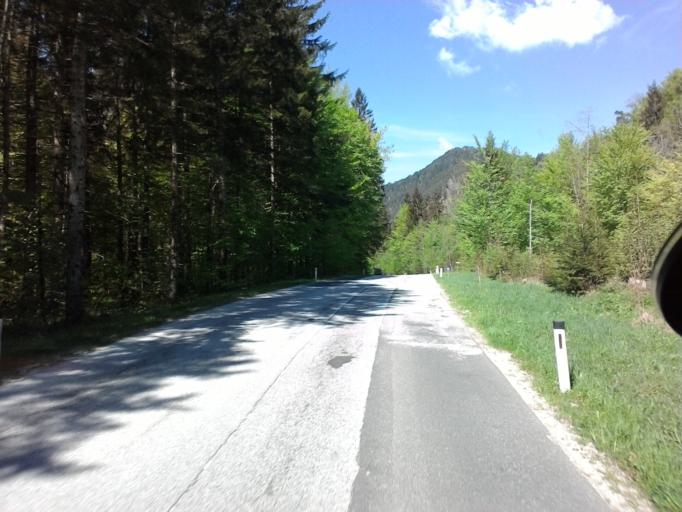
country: AT
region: Styria
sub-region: Politischer Bezirk Liezen
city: Wildalpen
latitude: 47.6721
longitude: 14.9709
